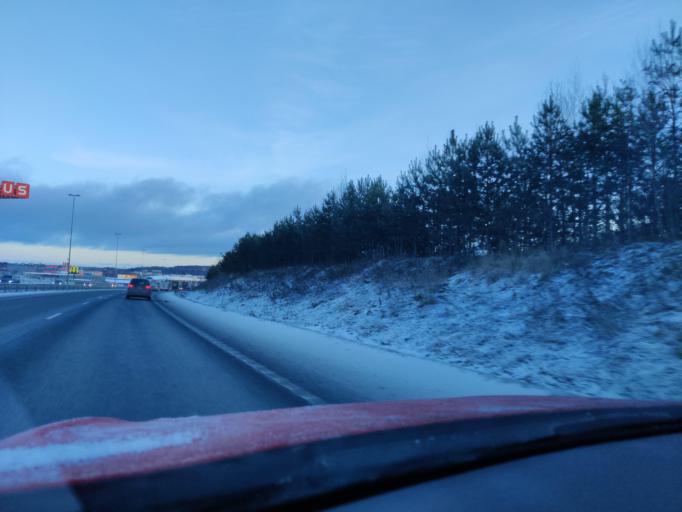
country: FI
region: Pirkanmaa
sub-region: Tampere
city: Tampere
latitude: 61.4639
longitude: 23.7141
